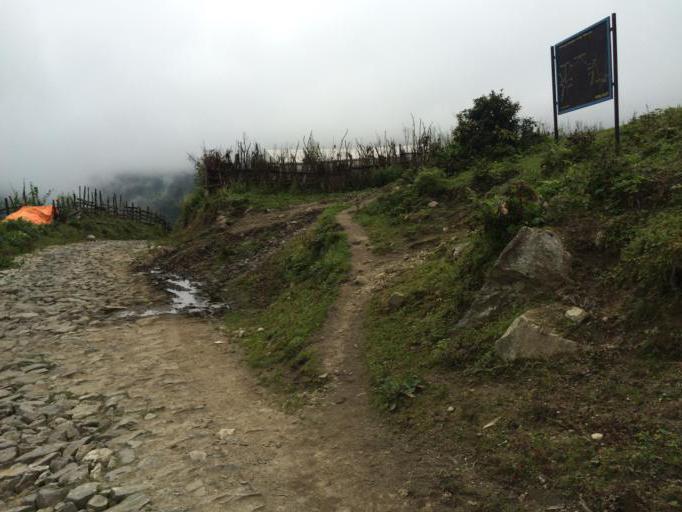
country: NP
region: Western Region
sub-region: Gandaki Zone
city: Chame
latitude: 28.5265
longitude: 84.3055
